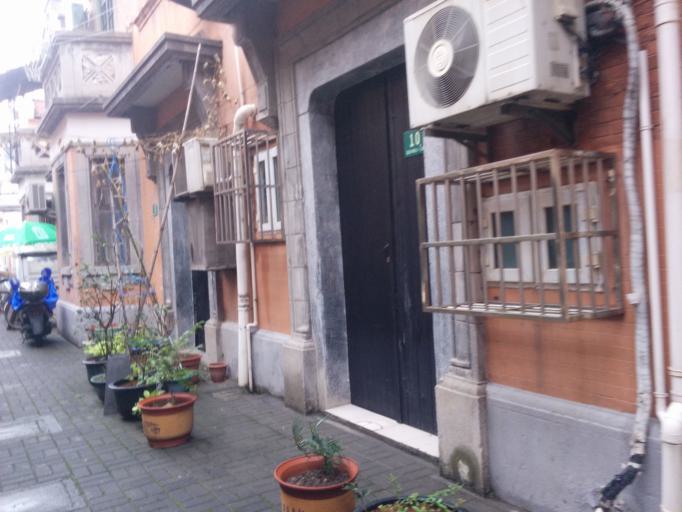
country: CN
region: Shanghai Shi
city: Shanghai
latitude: 31.2245
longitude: 121.4487
